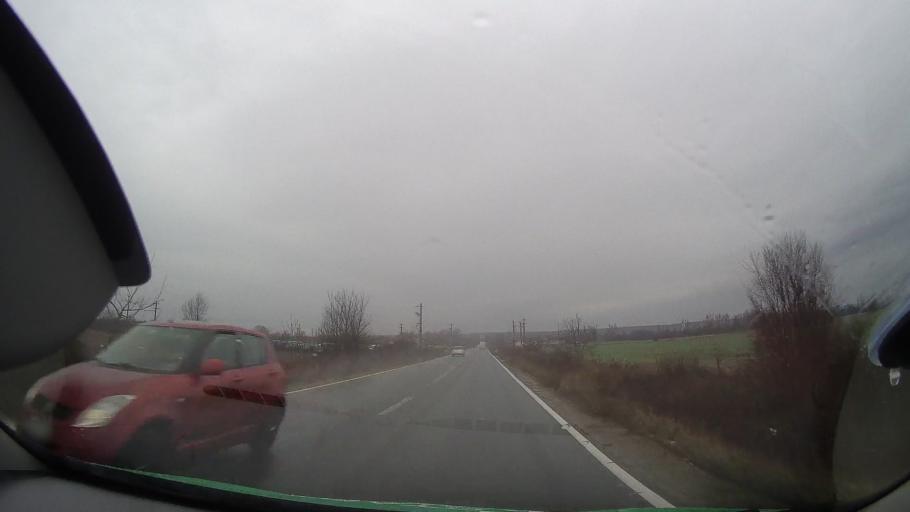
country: RO
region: Bihor
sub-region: Comuna Tinca
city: Tinca
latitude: 46.7621
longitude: 21.9345
